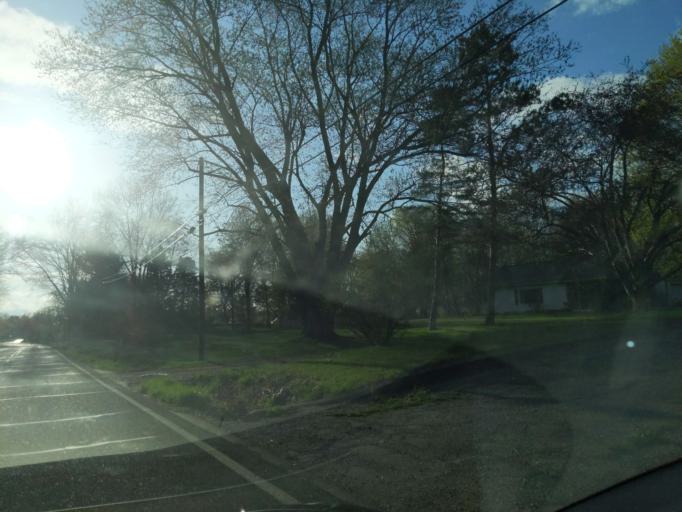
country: US
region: Michigan
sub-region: Ingham County
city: Leslie
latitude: 42.3930
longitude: -84.4600
